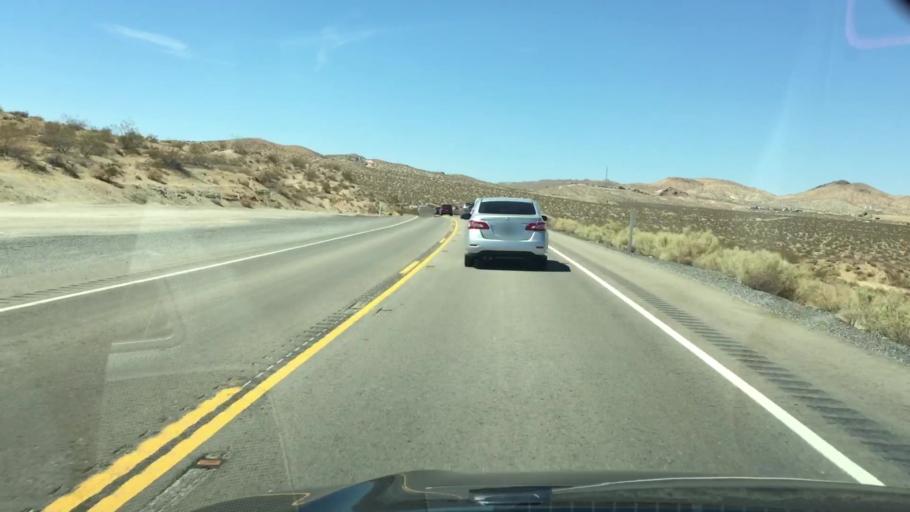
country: US
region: California
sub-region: Kern County
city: Ridgecrest
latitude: 35.3259
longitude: -117.6138
